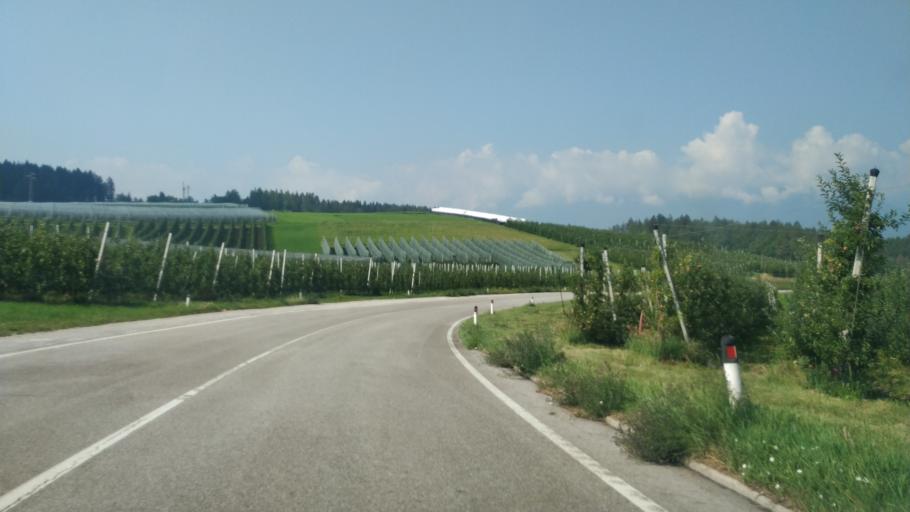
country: IT
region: Trentino-Alto Adige
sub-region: Provincia di Trento
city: Romeno
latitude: 46.3899
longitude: 11.1152
